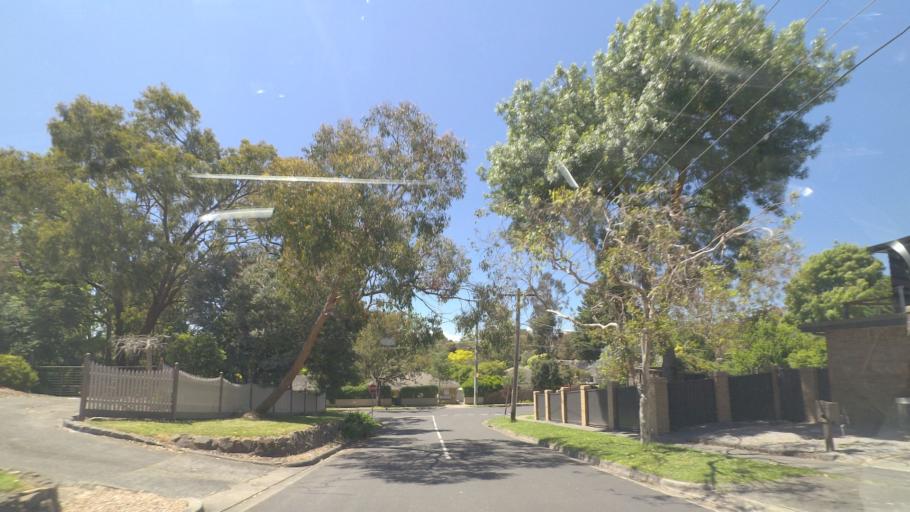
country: AU
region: Victoria
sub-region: Maroondah
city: Croydon North
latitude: -37.7759
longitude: 145.2847
